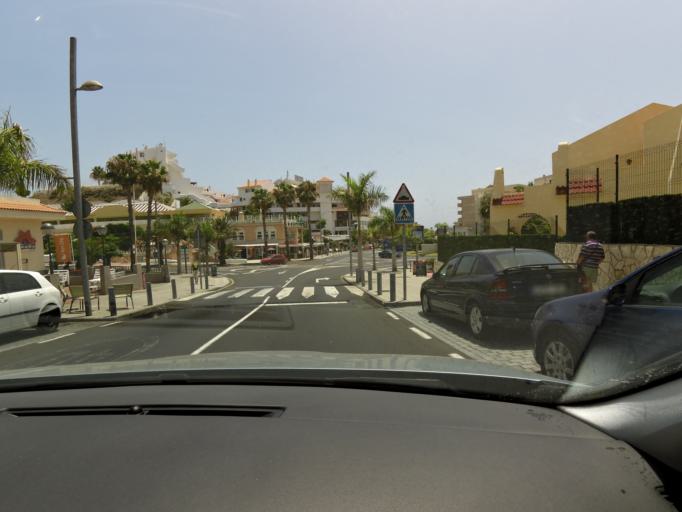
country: ES
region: Canary Islands
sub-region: Provincia de Santa Cruz de Tenerife
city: Playa de las Americas
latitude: 28.0854
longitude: -16.7319
